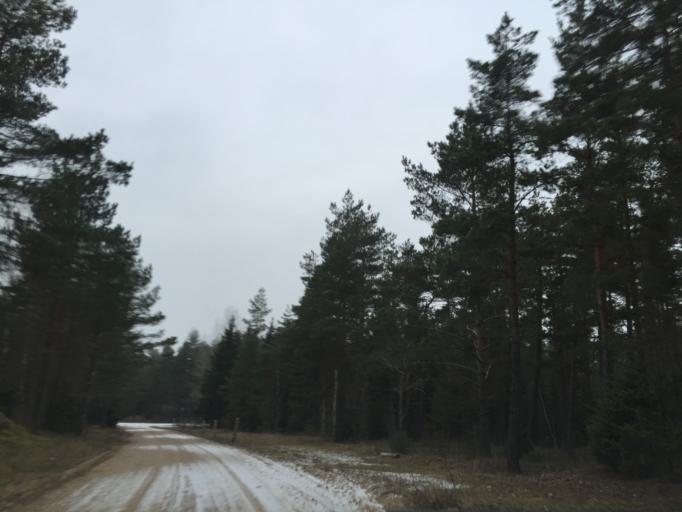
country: EE
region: Saare
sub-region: Kuressaare linn
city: Kuressaare
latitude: 58.4070
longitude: 22.2007
